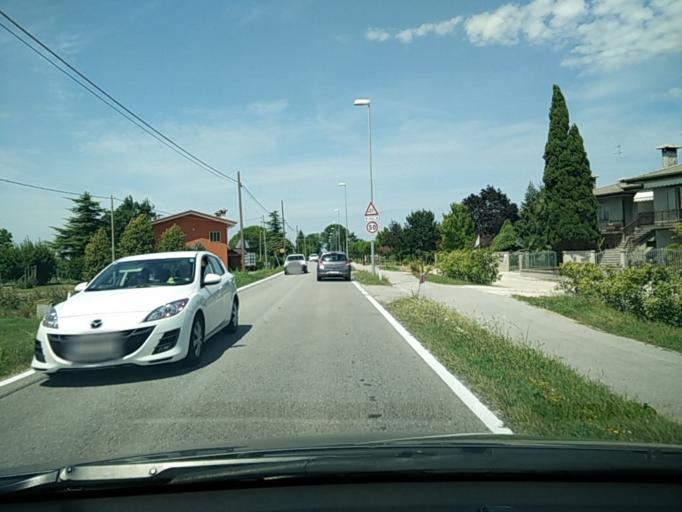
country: IT
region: Veneto
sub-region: Provincia di Venezia
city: Passarella
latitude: 45.5713
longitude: 12.6213
